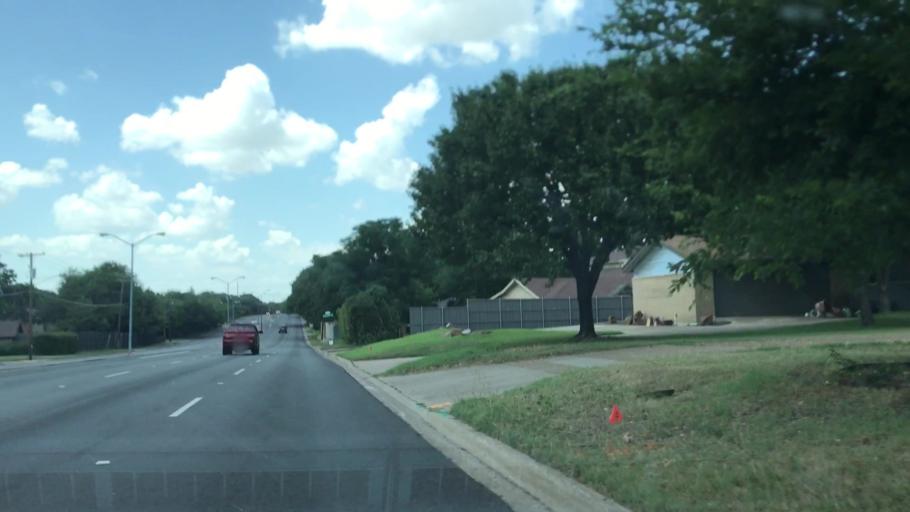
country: US
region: Texas
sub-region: Dallas County
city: Addison
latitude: 32.9052
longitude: -96.8382
